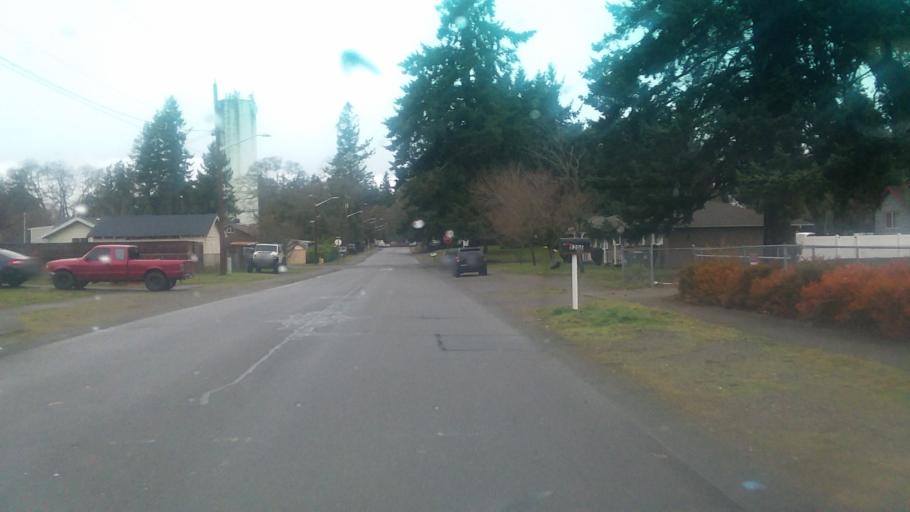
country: US
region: Washington
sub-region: Pierce County
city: Fort Lewis
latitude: 47.1258
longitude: -122.5482
